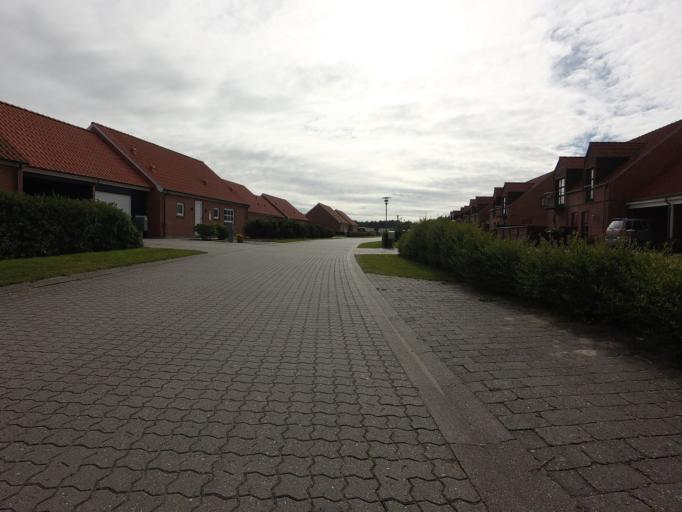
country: DK
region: North Denmark
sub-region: Jammerbugt Kommune
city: Pandrup
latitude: 57.3640
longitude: 9.7180
